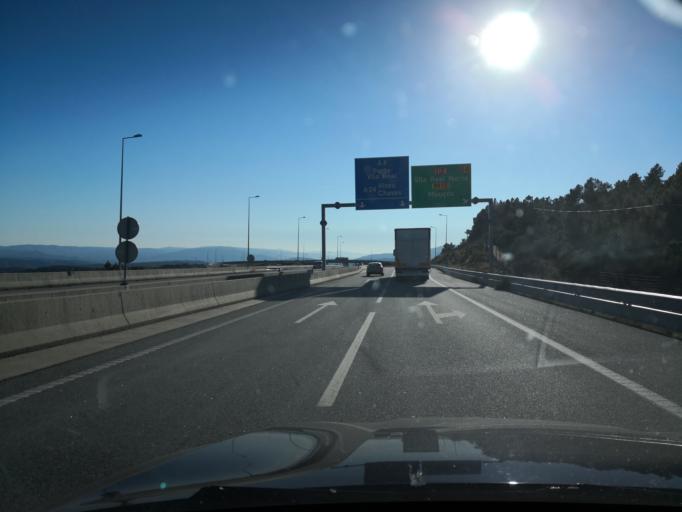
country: PT
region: Vila Real
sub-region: Vila Real
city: Vila Real
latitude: 41.3207
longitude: -7.6564
